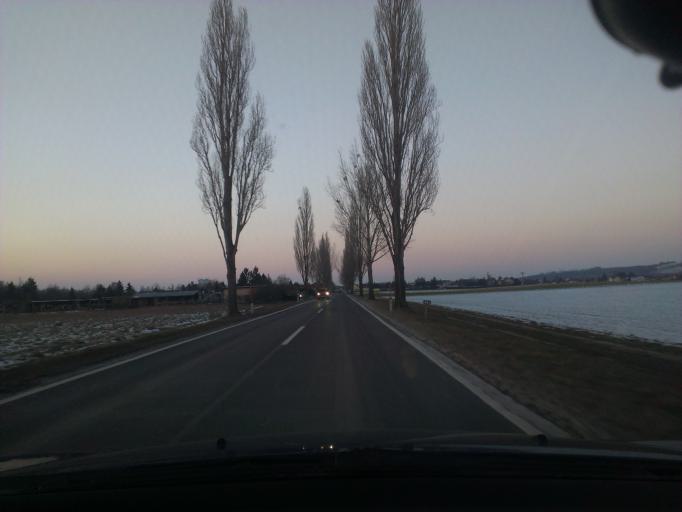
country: AT
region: Lower Austria
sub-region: Politischer Bezirk Bruck an der Leitha
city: Enzersdorf an der Fischa
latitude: 48.0724
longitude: 16.6089
